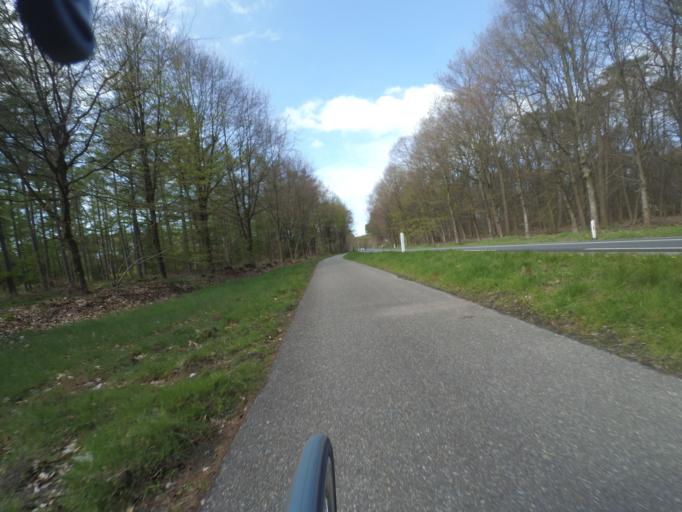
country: NL
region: Gelderland
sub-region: Gemeente Oldebroek
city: Oldebroek
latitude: 52.3564
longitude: 5.8766
